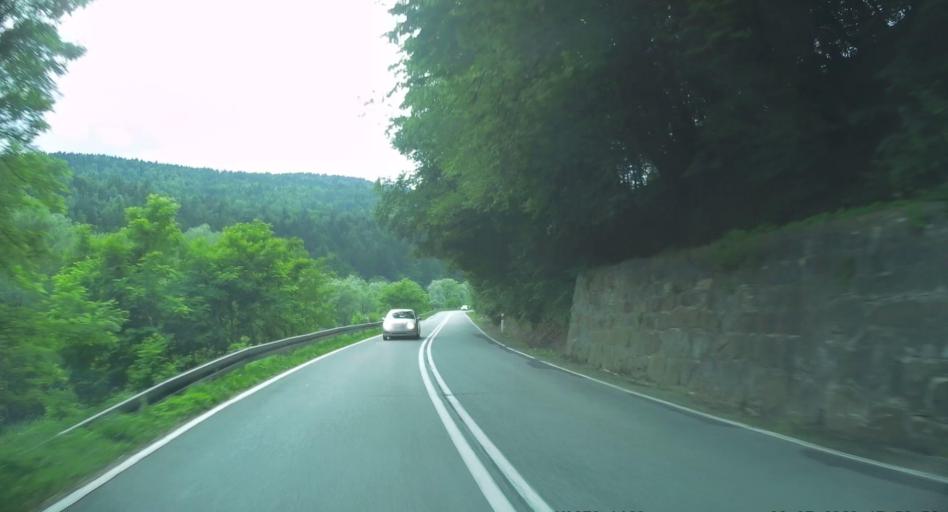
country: PL
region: Lesser Poland Voivodeship
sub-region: Powiat nowosadecki
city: Piwniczna-Zdroj
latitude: 49.3733
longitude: 20.7609
